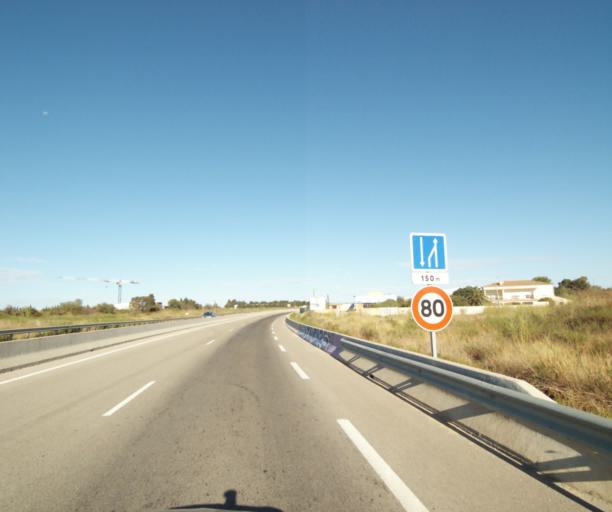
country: FR
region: Languedoc-Roussillon
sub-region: Departement du Gard
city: Bouillargues
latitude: 43.7886
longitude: 4.4352
